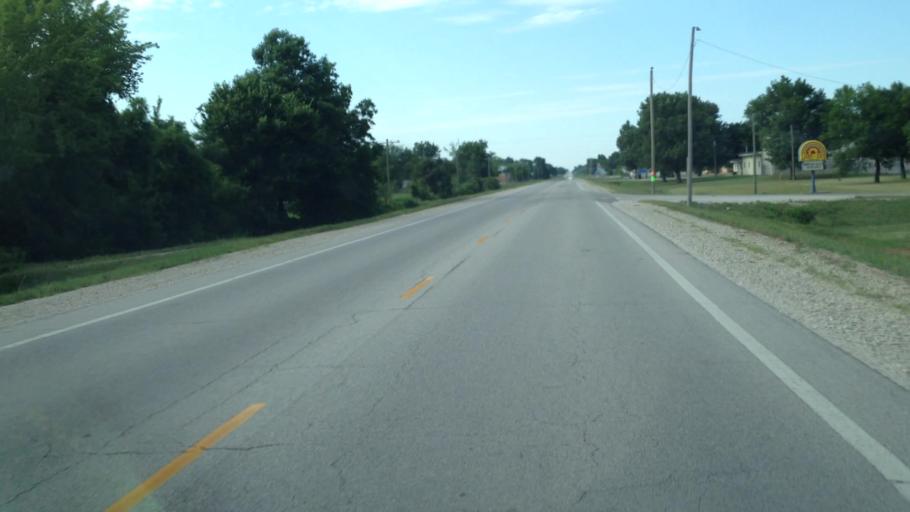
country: US
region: Kansas
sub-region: Neosho County
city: Erie
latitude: 37.5681
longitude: -95.2526
